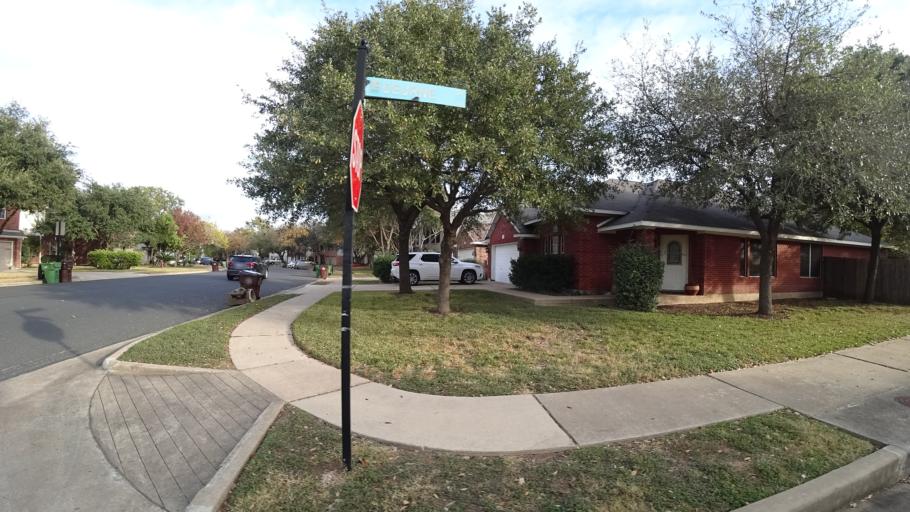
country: US
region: Texas
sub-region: Williamson County
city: Brushy Creek
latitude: 30.5128
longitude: -97.7287
